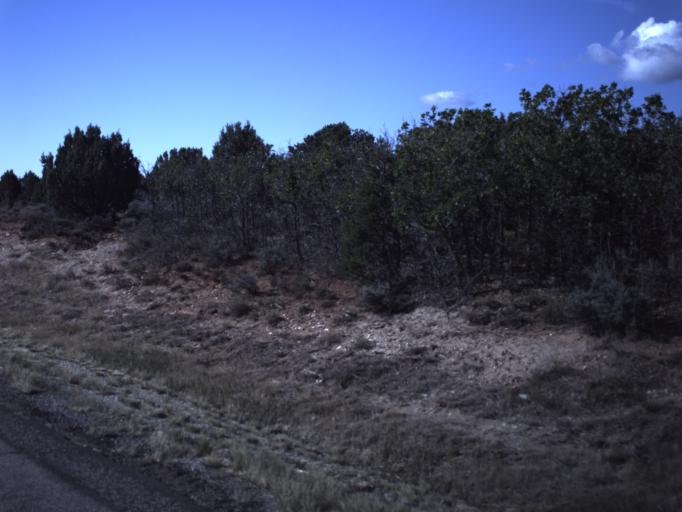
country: US
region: Utah
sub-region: San Juan County
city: Monticello
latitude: 37.9061
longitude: -109.3455
